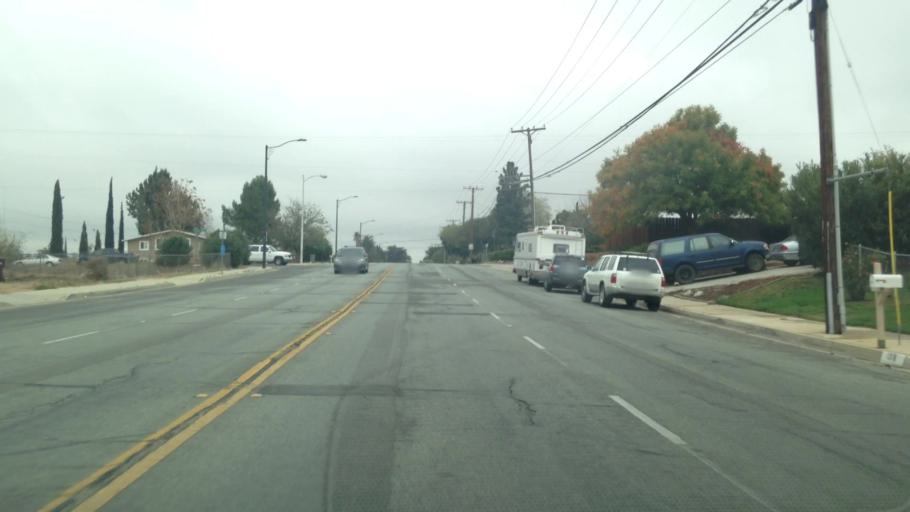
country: US
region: California
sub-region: Riverside County
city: Beaumont
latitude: 33.9443
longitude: -116.9773
